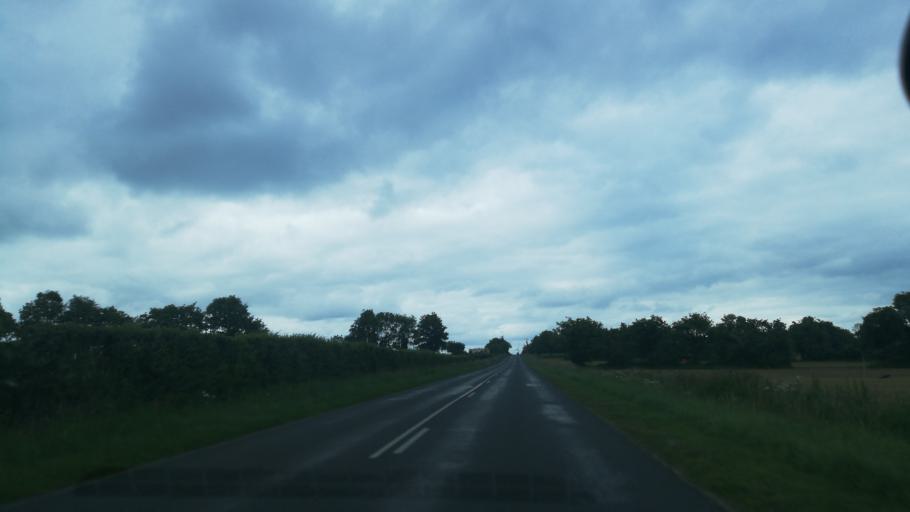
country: FR
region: Poitou-Charentes
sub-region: Departement des Deux-Sevres
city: Courlay
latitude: 46.7604
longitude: -0.5368
